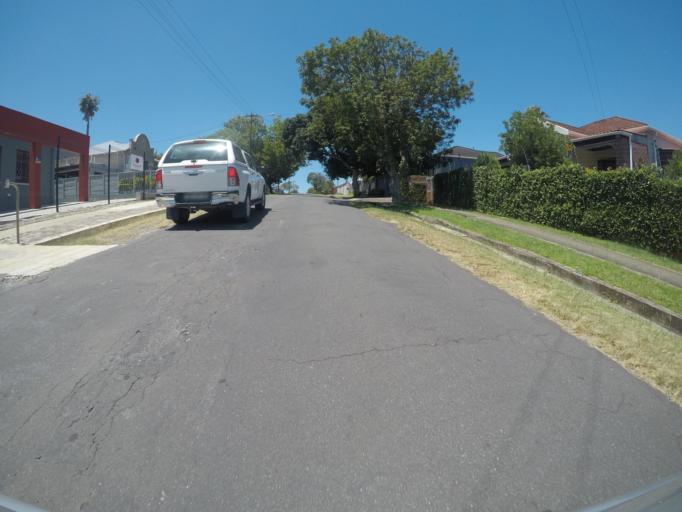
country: ZA
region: Eastern Cape
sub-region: Buffalo City Metropolitan Municipality
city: East London
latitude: -32.9885
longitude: 27.9028
